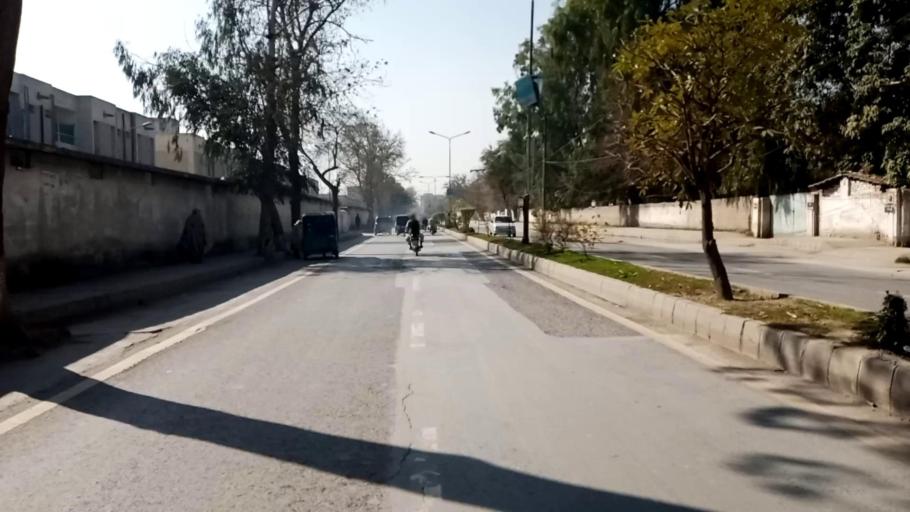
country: PK
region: Khyber Pakhtunkhwa
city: Peshawar
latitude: 33.9881
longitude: 71.5315
